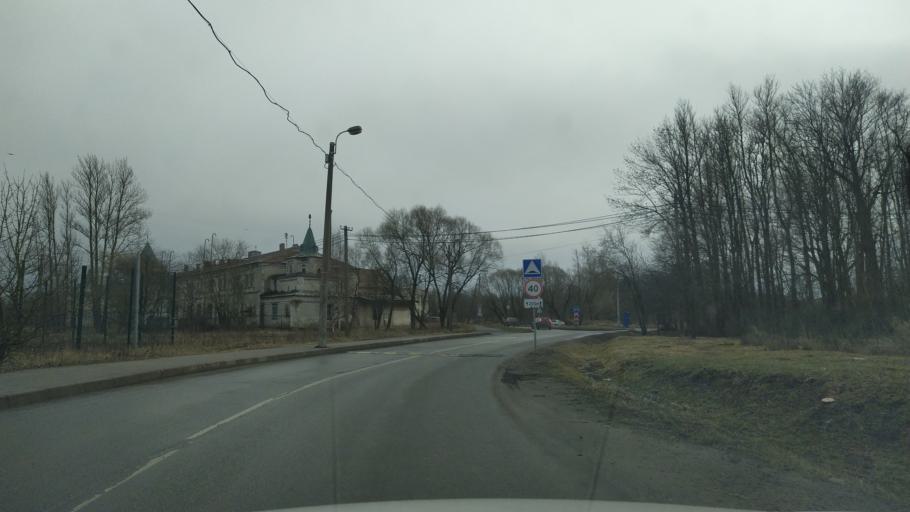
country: RU
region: St.-Petersburg
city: Pushkin
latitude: 59.7303
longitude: 30.3851
